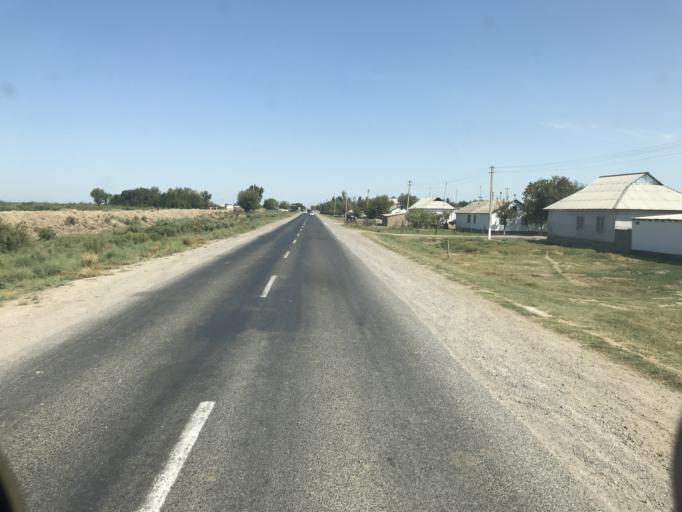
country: KZ
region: Ongtustik Qazaqstan
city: Myrzakent
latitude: 40.7561
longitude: 68.5370
